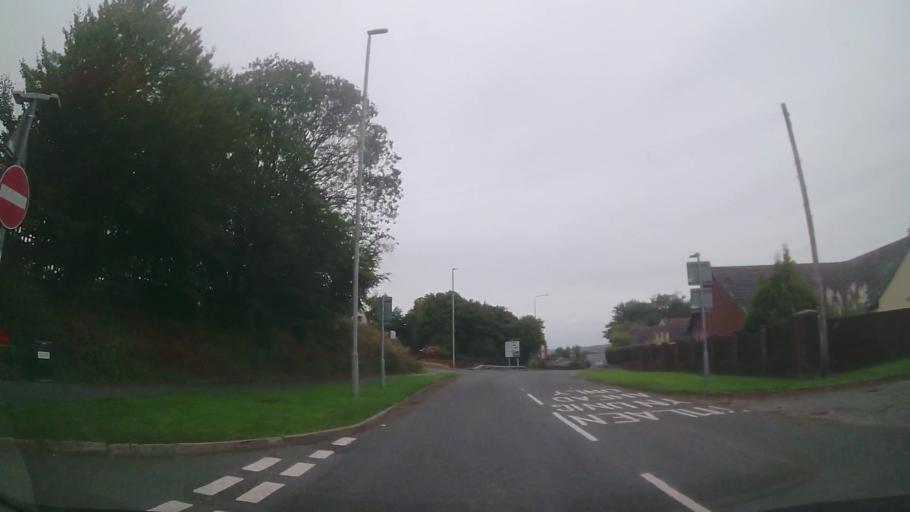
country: GB
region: Wales
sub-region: Carmarthenshire
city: Saint Clears
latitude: 51.8164
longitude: -4.4979
